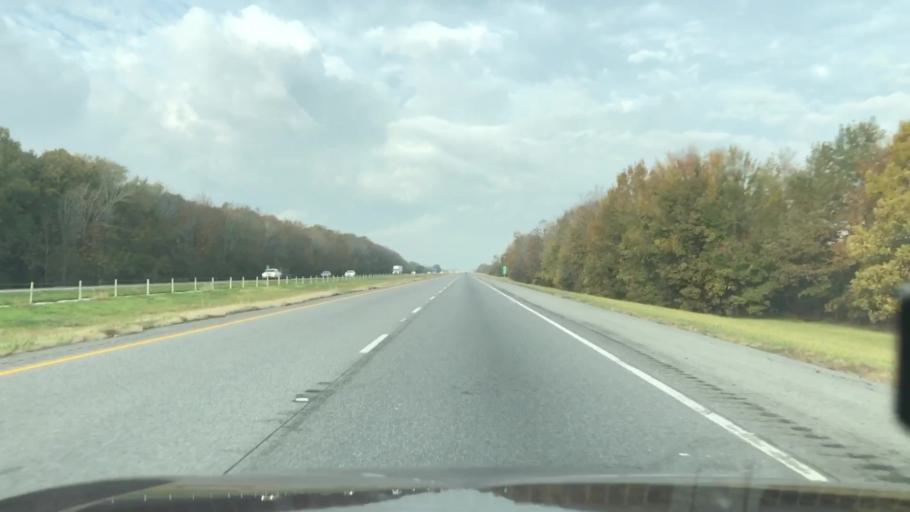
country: US
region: Louisiana
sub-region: Richland Parish
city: Delhi
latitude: 32.4262
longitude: -91.3837
